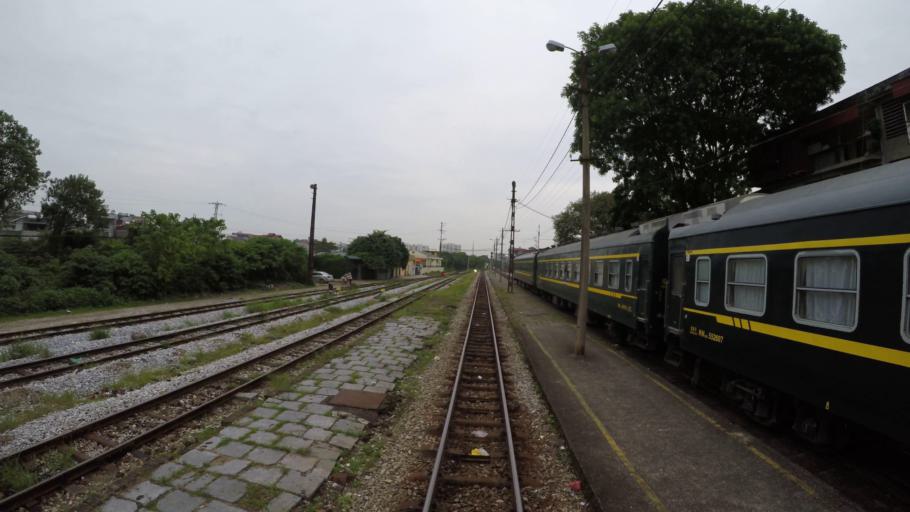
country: VN
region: Ha Noi
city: Trau Quy
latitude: 21.0264
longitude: 105.9240
